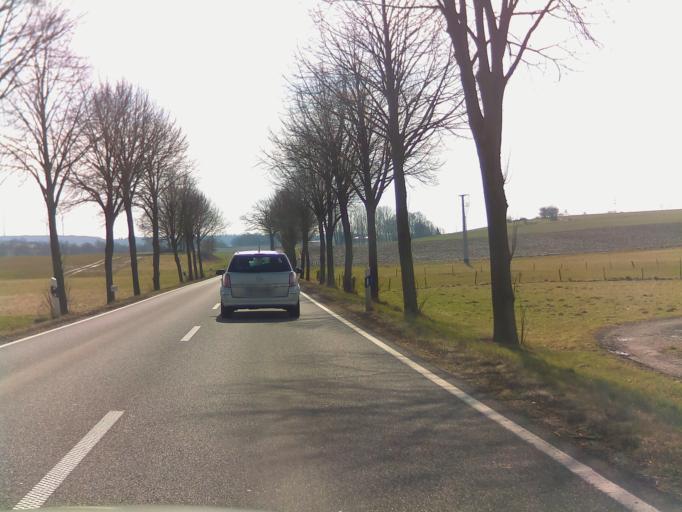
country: DE
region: Hesse
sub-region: Regierungsbezirk Giessen
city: Grunberg
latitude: 50.6182
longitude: 8.9413
